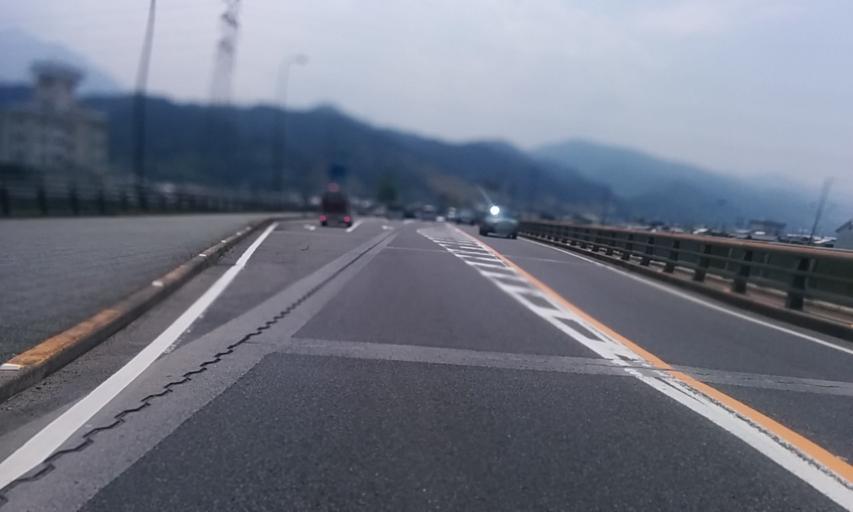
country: JP
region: Ehime
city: Saijo
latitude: 33.9032
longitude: 133.1840
